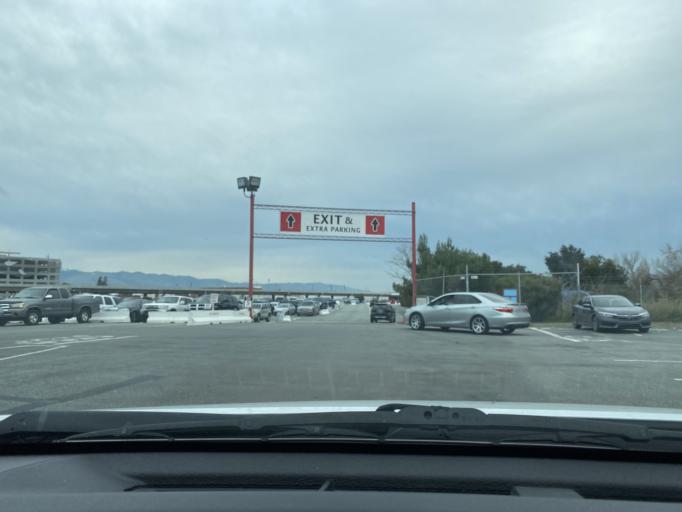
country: US
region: California
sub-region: Santa Clara County
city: San Jose
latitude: 37.3665
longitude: -121.8769
